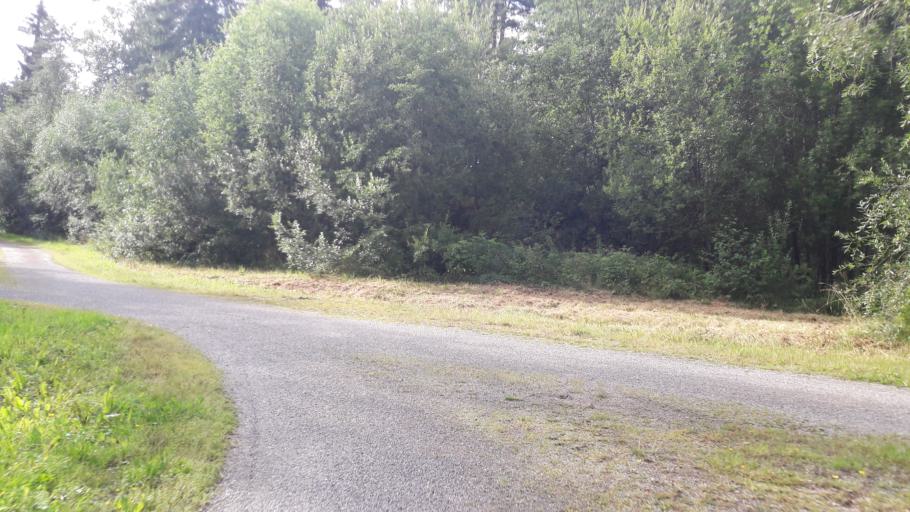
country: FI
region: North Karelia
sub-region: Joensuu
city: Joensuu
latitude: 62.5880
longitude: 29.7985
